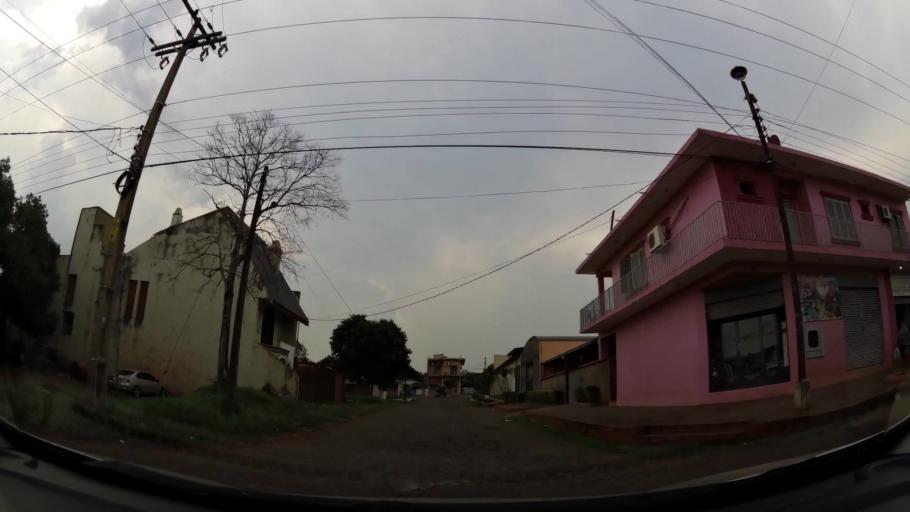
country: PY
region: Alto Parana
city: Presidente Franco
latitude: -25.5414
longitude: -54.6121
